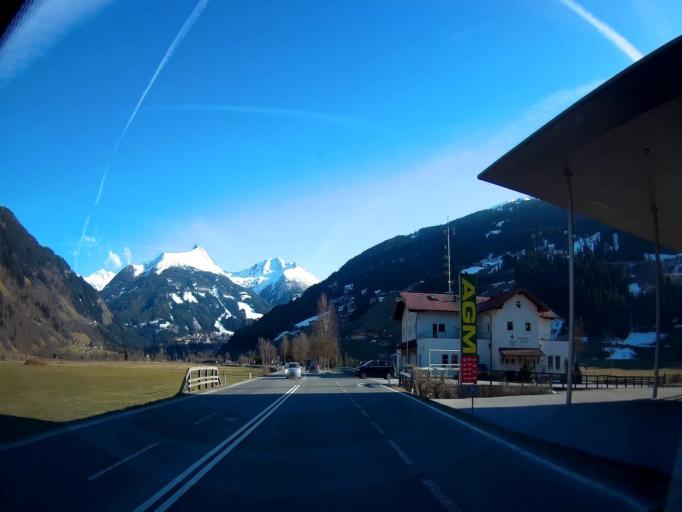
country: AT
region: Salzburg
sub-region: Politischer Bezirk Sankt Johann im Pongau
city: Bad Hofgastein
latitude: 47.1500
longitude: 13.1136
